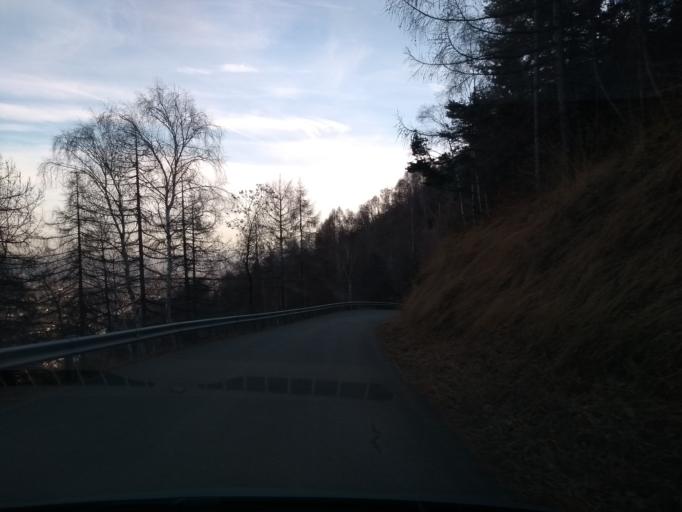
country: IT
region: Piedmont
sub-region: Provincia di Torino
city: Coassolo Torinese
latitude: 45.2809
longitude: 7.4523
